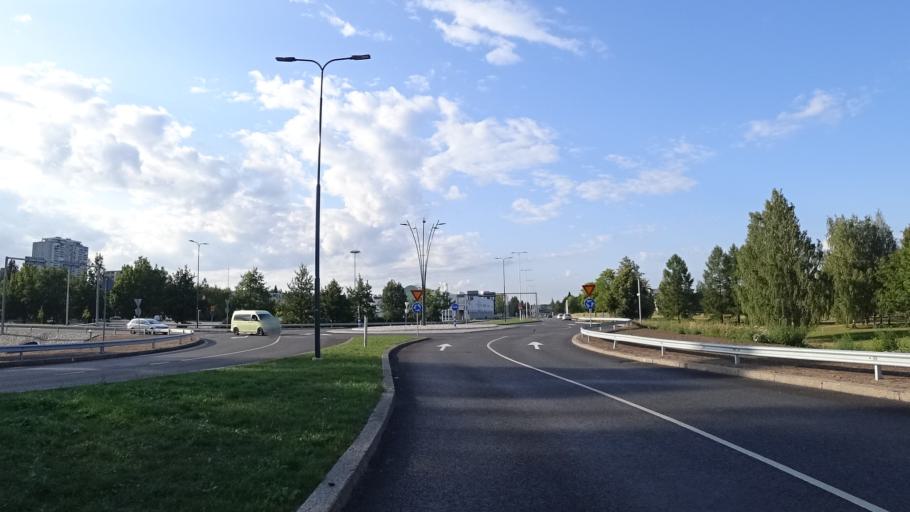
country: FI
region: South Karelia
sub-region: Imatra
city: Imatra
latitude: 61.1882
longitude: 28.7776
